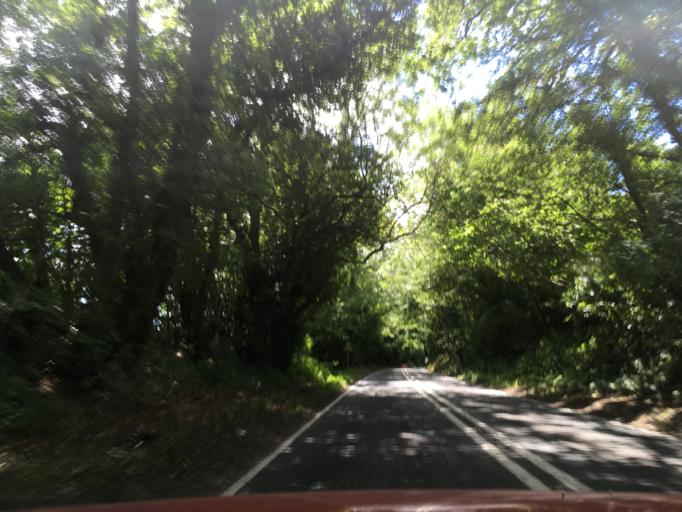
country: GB
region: England
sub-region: Hampshire
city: Highclere
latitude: 51.3176
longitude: -1.3831
